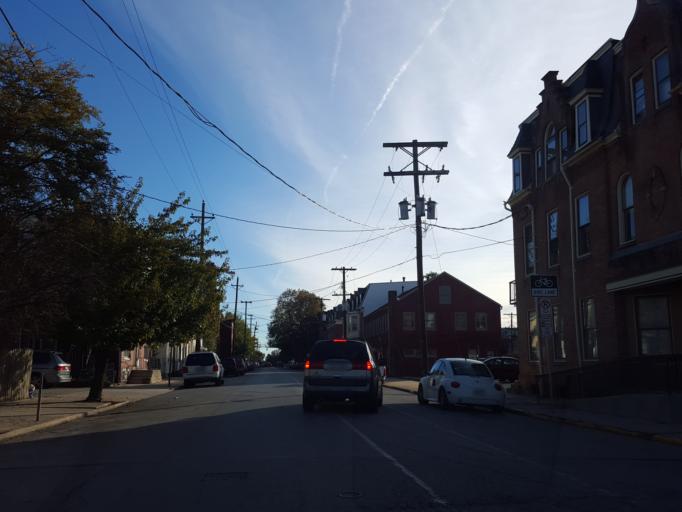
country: US
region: Pennsylvania
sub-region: York County
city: York
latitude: 39.9623
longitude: -76.7230
